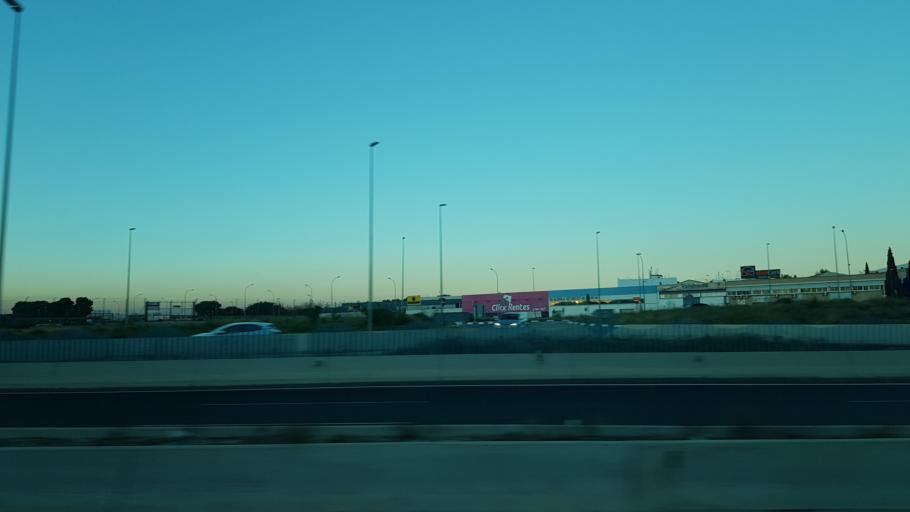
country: ES
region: Valencia
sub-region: Provincia de Valencia
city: Manises
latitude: 39.4814
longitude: -0.4596
